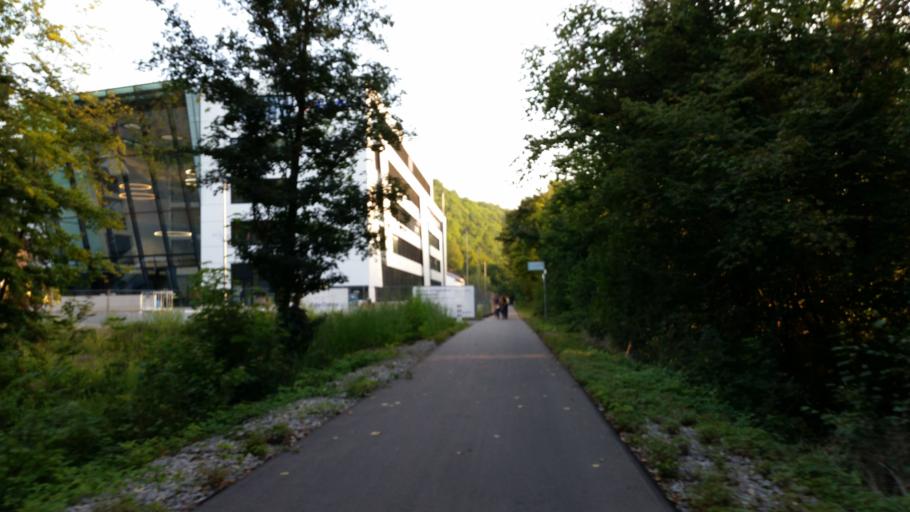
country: DE
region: Baden-Wuerttemberg
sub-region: Regierungsbezirk Stuttgart
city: Marbach am Neckar
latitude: 48.9342
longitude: 9.2513
